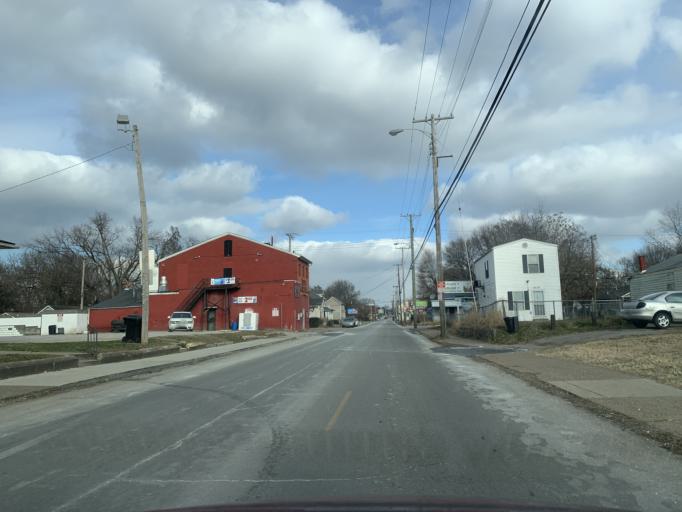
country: US
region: Kentucky
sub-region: Jefferson County
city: Louisville
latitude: 38.2560
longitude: -85.7942
